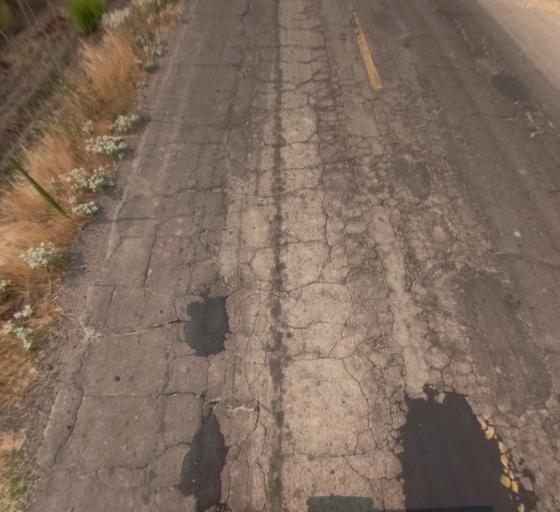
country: US
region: California
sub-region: Madera County
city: Fairmead
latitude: 37.0956
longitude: -120.1108
